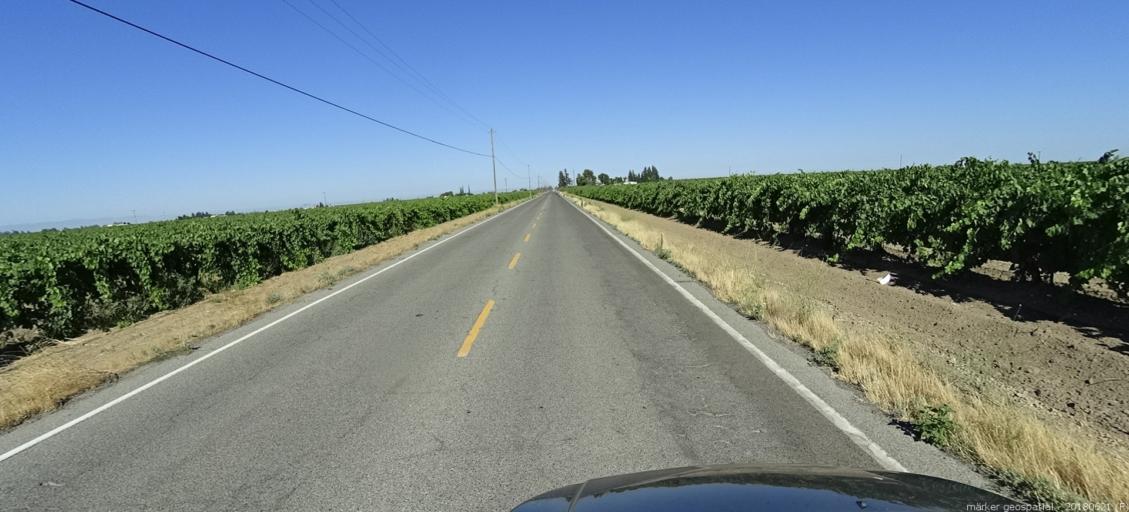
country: US
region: California
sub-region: Fresno County
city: Biola
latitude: 36.8513
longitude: -120.0248
